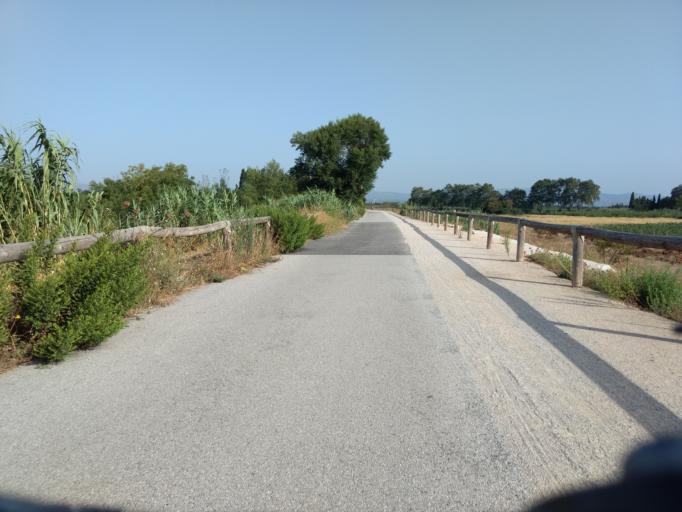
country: FR
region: Languedoc-Roussillon
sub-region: Departement des Pyrenees-Orientales
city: Claira
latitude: 42.7579
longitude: 2.9362
